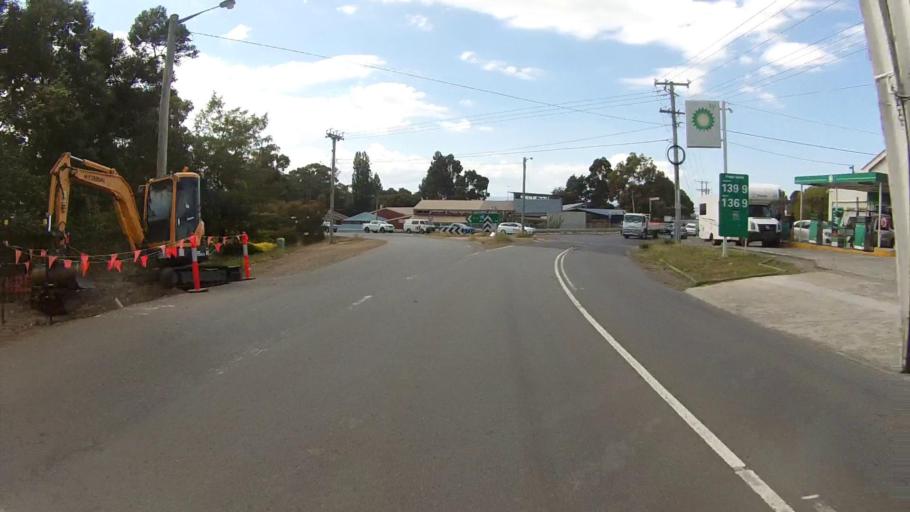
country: AU
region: Tasmania
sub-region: Clarence
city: Cambridge
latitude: -42.8370
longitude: 147.4402
